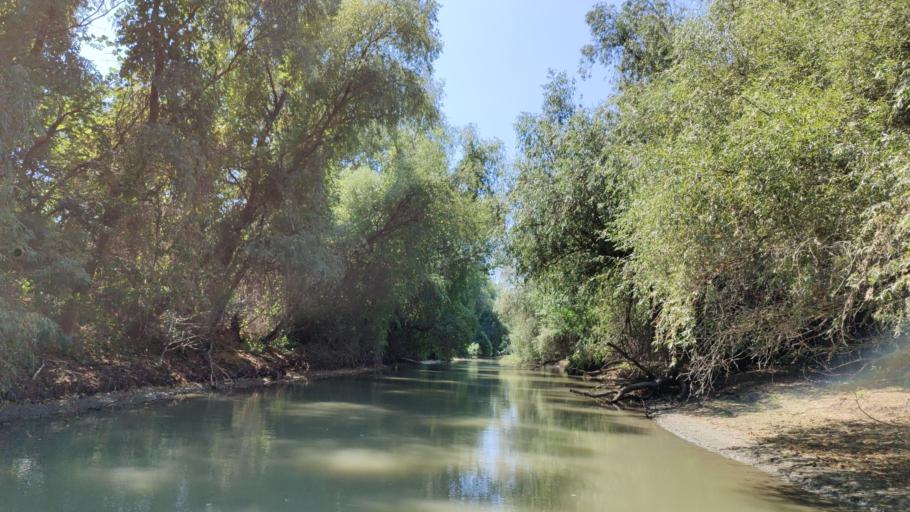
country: RO
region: Tulcea
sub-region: Comuna Pardina
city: Pardina
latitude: 45.2551
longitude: 28.9835
